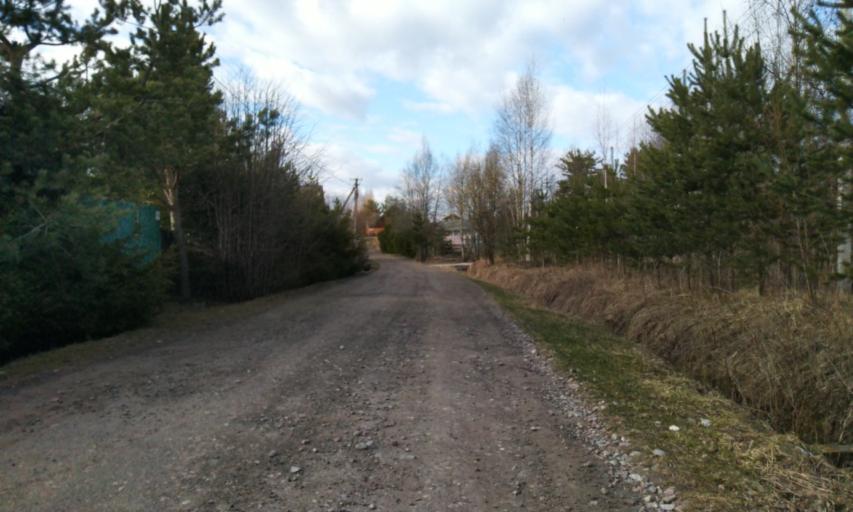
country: RU
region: Leningrad
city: Toksovo
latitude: 60.1274
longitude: 30.4893
